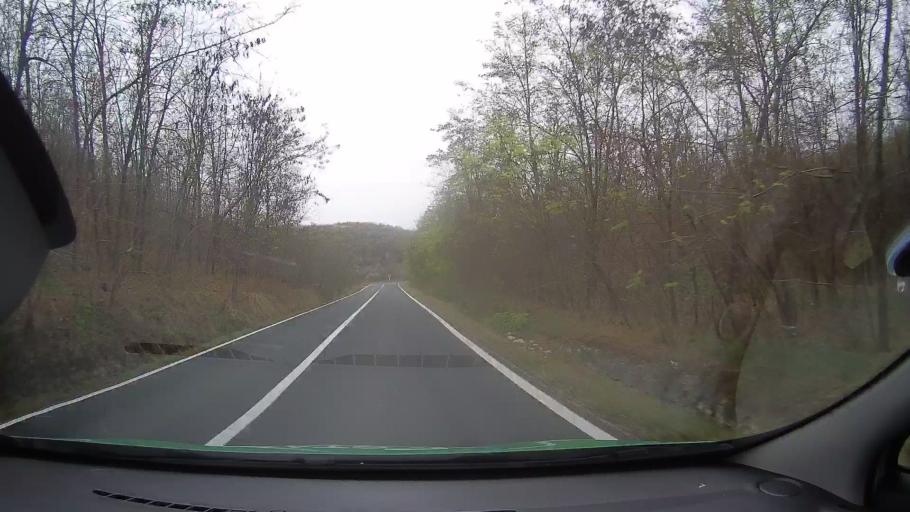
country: RO
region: Constanta
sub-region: Comuna Garliciu
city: Garliciu
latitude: 44.7065
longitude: 28.0712
